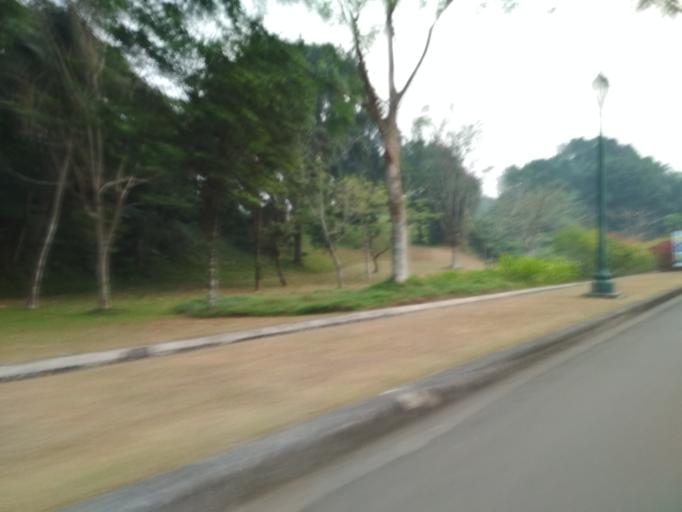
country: ID
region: West Java
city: Caringin
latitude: -6.6622
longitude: 106.8354
